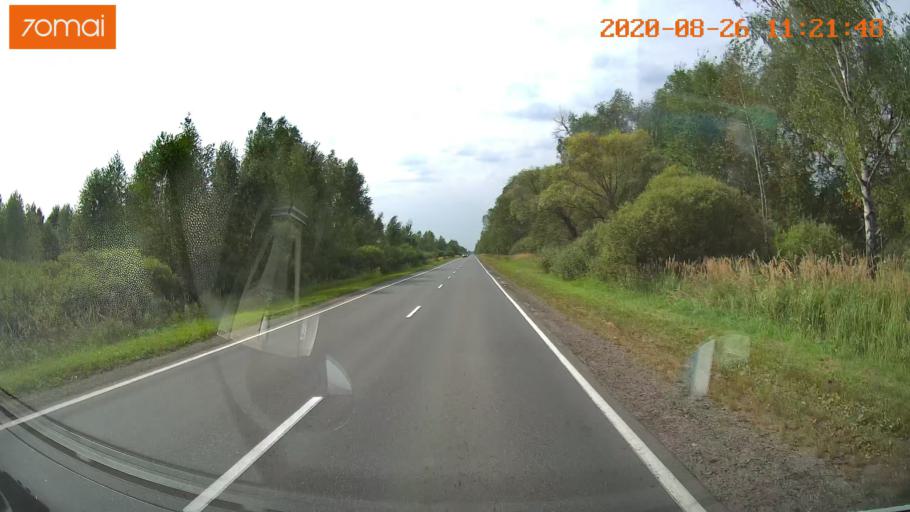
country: RU
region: Rjazan
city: Shilovo
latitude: 54.3718
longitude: 41.0385
